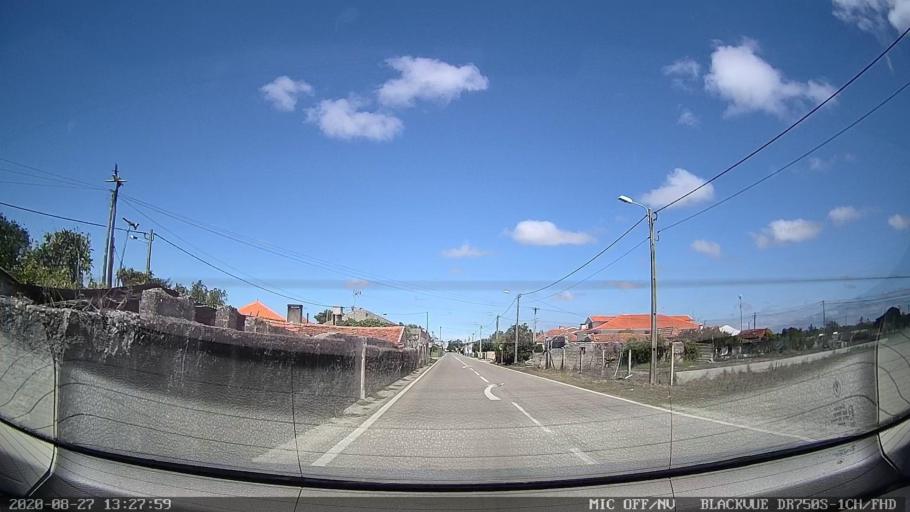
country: PT
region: Aveiro
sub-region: Vagos
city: Vagos
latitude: 40.5250
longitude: -8.6793
